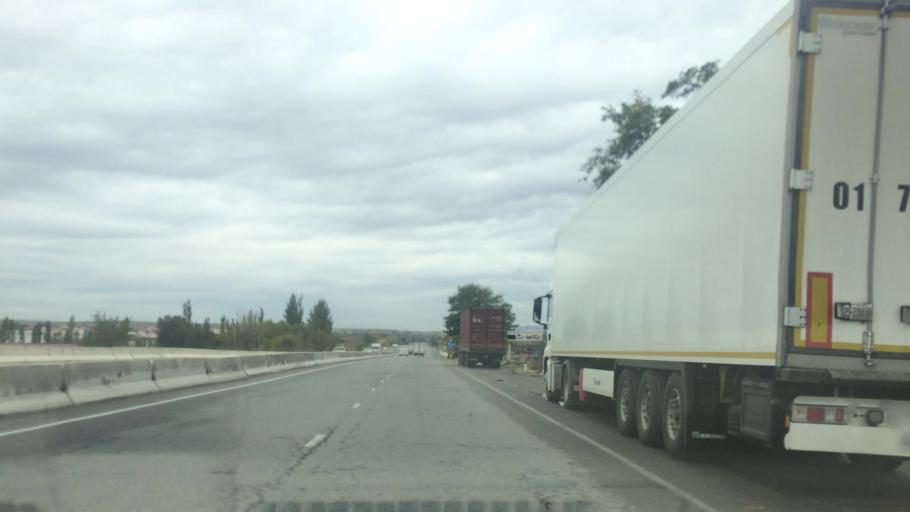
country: UZ
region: Jizzax
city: Jizzax
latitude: 39.9725
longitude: 67.5591
